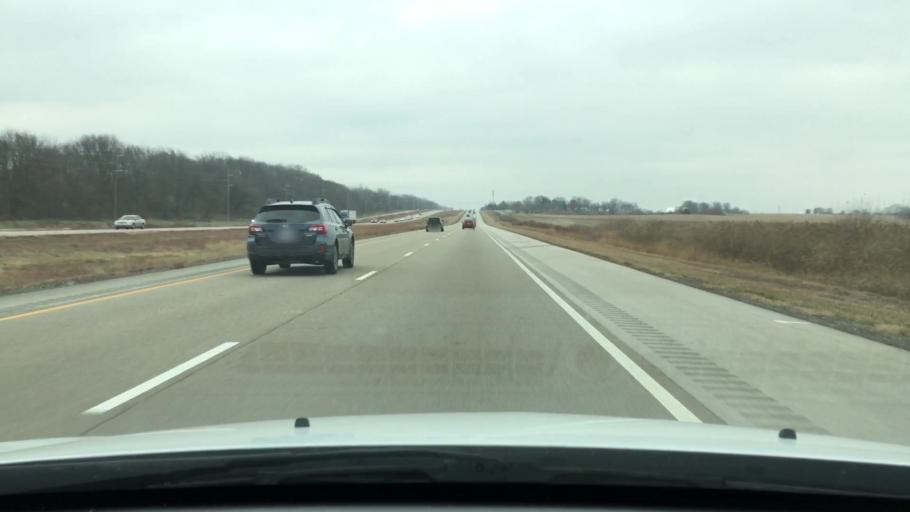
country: US
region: Illinois
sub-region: Logan County
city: Atlanta
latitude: 40.2307
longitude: -89.2656
